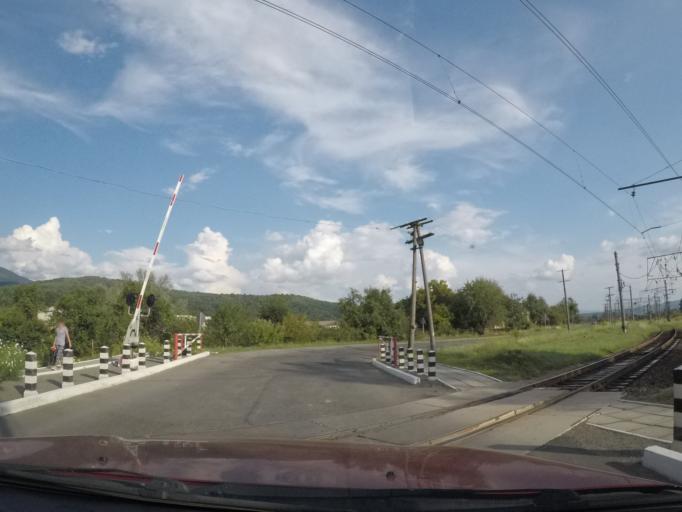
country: UA
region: Zakarpattia
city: Velykyi Bereznyi
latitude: 48.9078
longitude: 22.4582
